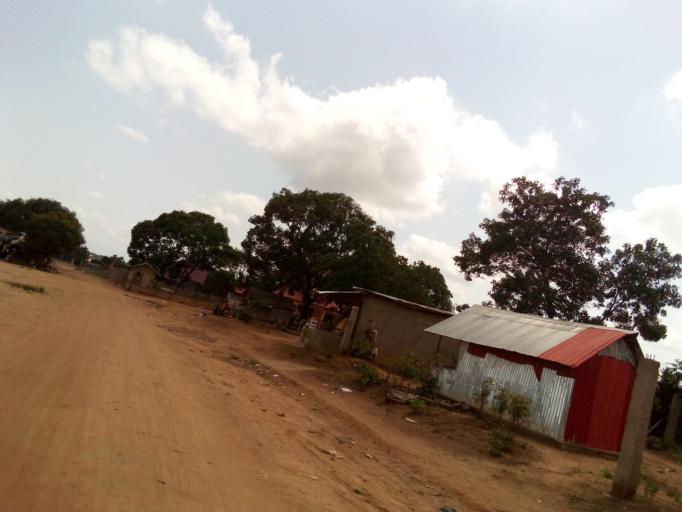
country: SL
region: Western Area
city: Waterloo
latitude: 8.3370
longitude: -13.0195
